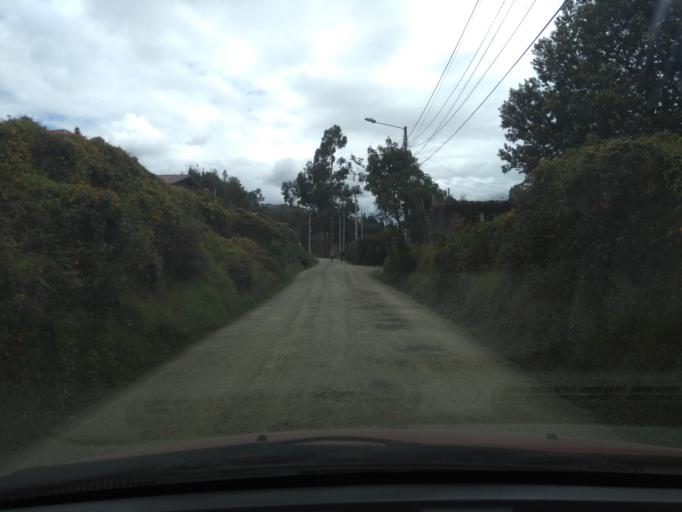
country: EC
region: Azuay
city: Llacao
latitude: -2.8509
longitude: -78.9152
